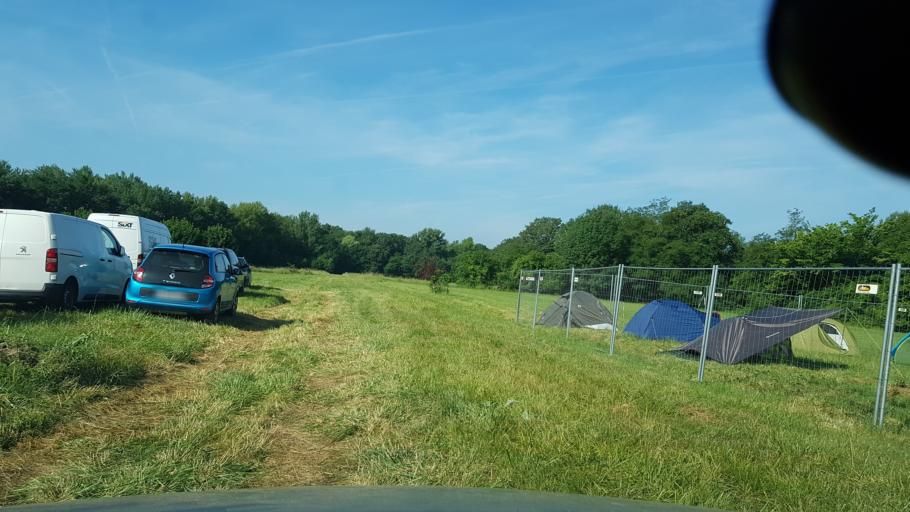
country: FR
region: Centre
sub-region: Departement du Loir-et-Cher
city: Selles-sur-Cher
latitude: 47.2737
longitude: 1.5485
